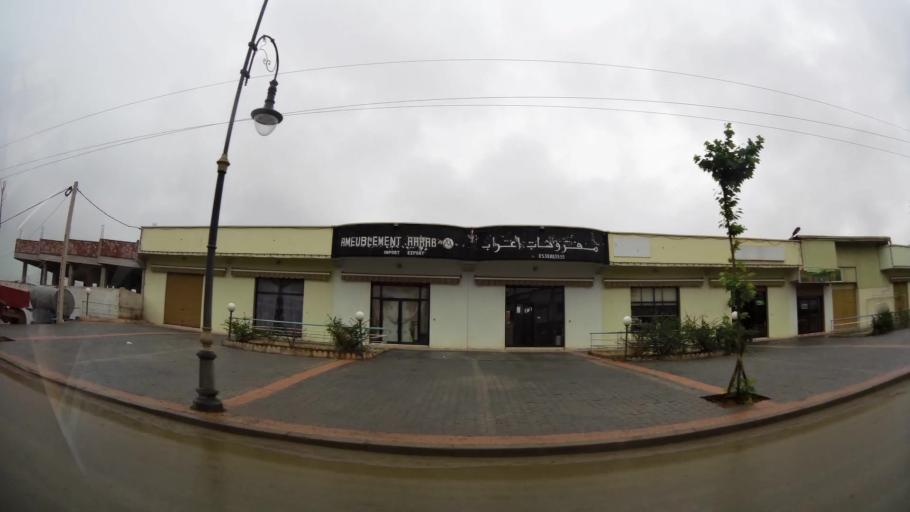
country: MA
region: Taza-Al Hoceima-Taounate
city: Imzourene
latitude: 35.1653
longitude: -3.8567
